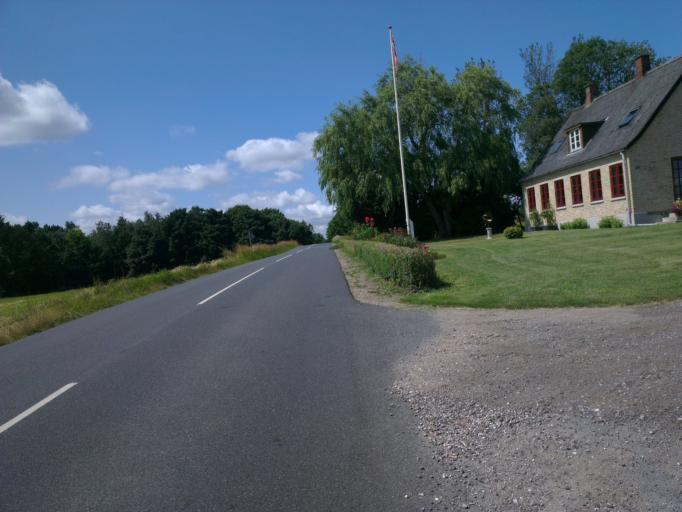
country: DK
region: Capital Region
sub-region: Frederikssund Kommune
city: Skibby
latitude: 55.7667
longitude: 11.9009
